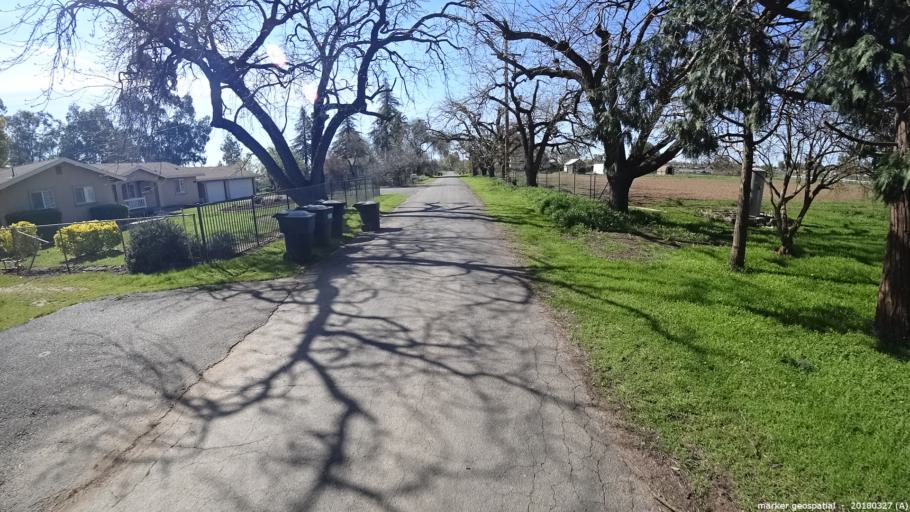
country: US
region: California
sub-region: Sacramento County
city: Vineyard
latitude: 38.4917
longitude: -121.3627
